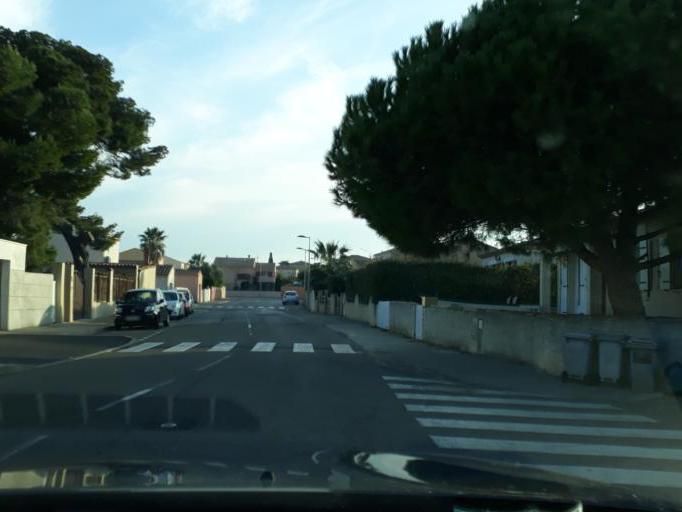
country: FR
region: Languedoc-Roussillon
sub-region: Departement de l'Herault
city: Marseillan
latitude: 43.3512
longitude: 3.5298
